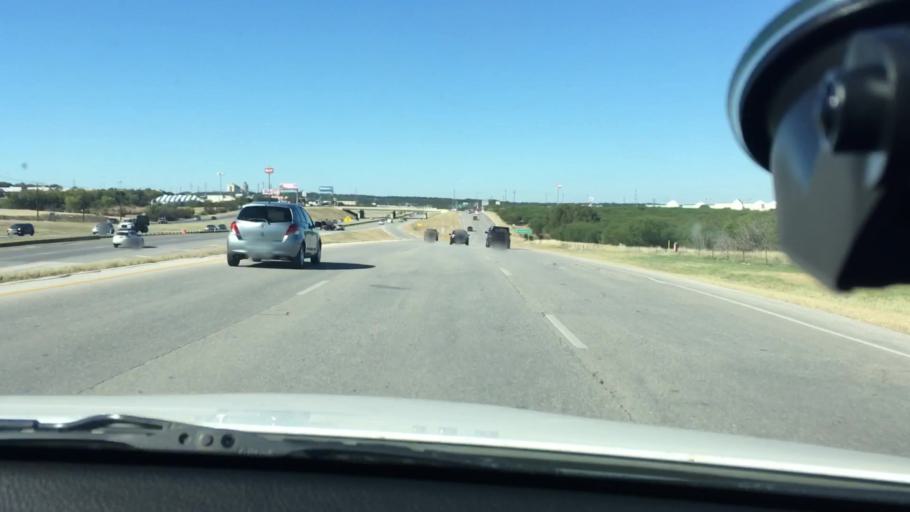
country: US
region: Texas
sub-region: Bexar County
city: Live Oak
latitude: 29.5866
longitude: -98.3479
